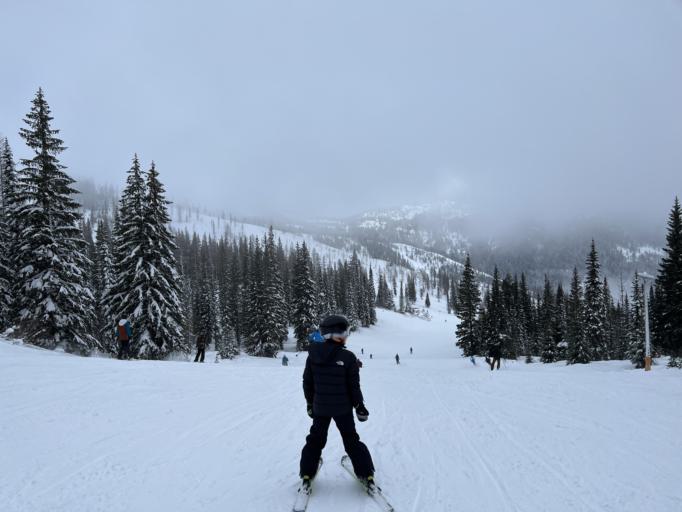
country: US
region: Idaho
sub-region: Bonner County
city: Ponderay
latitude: 48.3811
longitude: -116.6184
